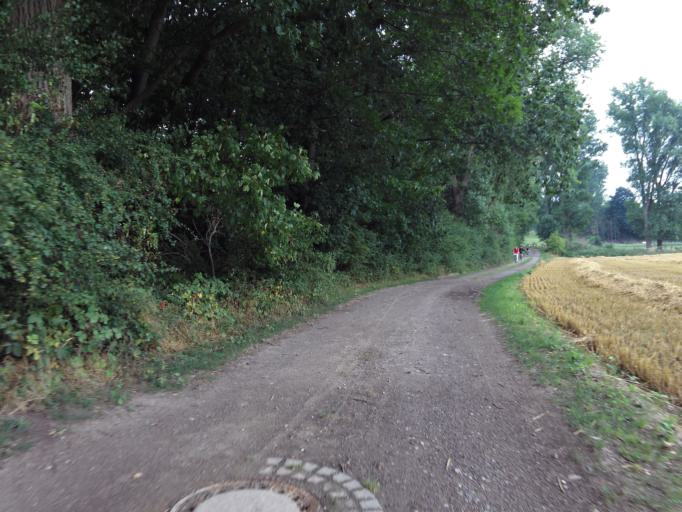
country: DE
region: North Rhine-Westphalia
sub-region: Regierungsbezirk Koln
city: Linnich
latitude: 50.9650
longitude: 6.2594
